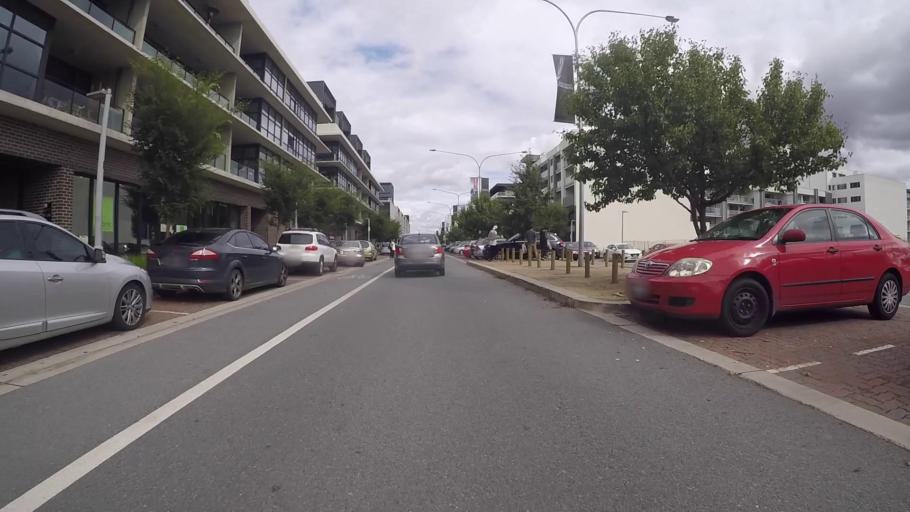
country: AU
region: Australian Capital Territory
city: Forrest
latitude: -35.3120
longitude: 149.1459
